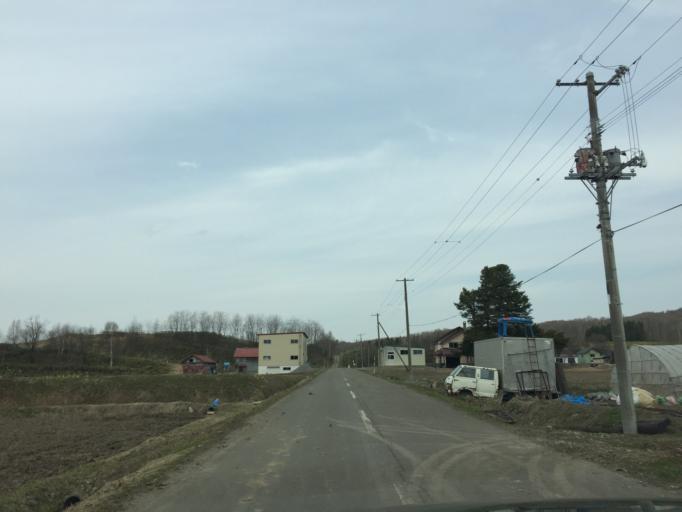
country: JP
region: Hokkaido
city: Ashibetsu
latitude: 43.6173
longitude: 142.2151
